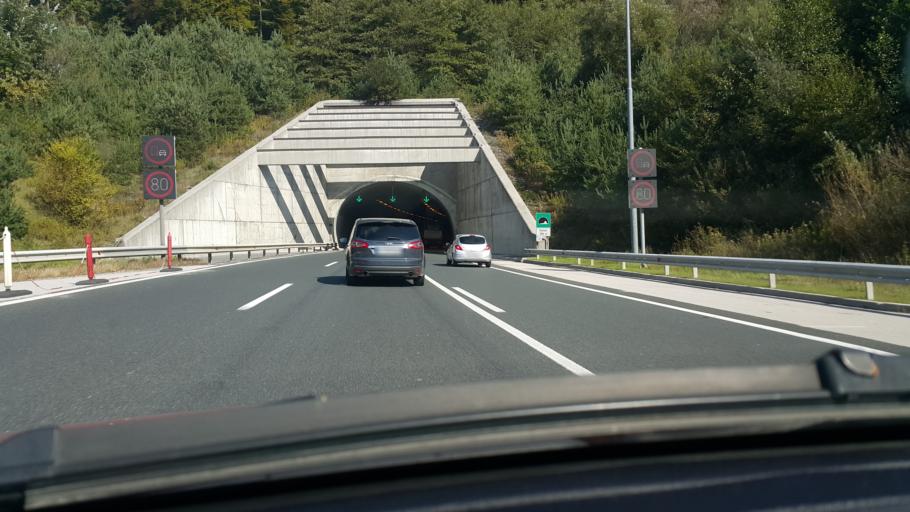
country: SI
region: Skofljica
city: Lavrica
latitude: 46.0172
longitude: 14.5587
